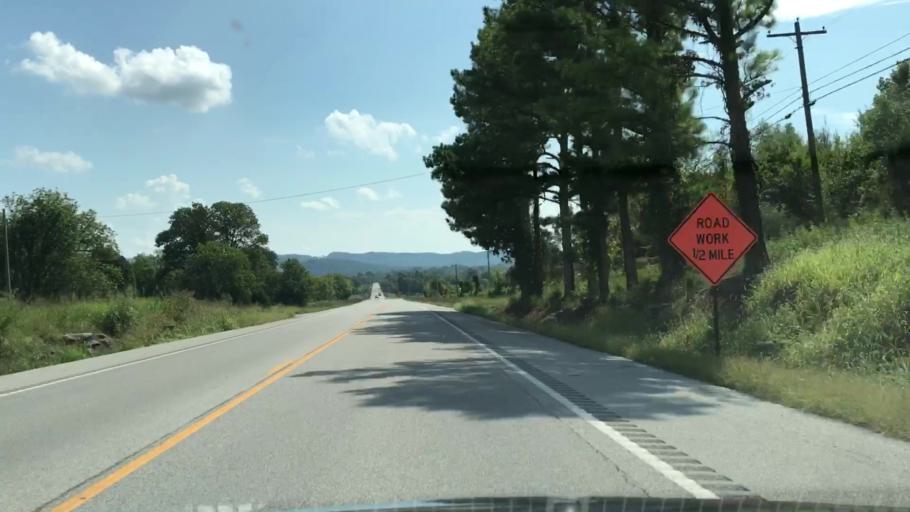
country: US
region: Tennessee
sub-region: Trousdale County
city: Hartsville
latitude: 36.3656
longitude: -86.0786
